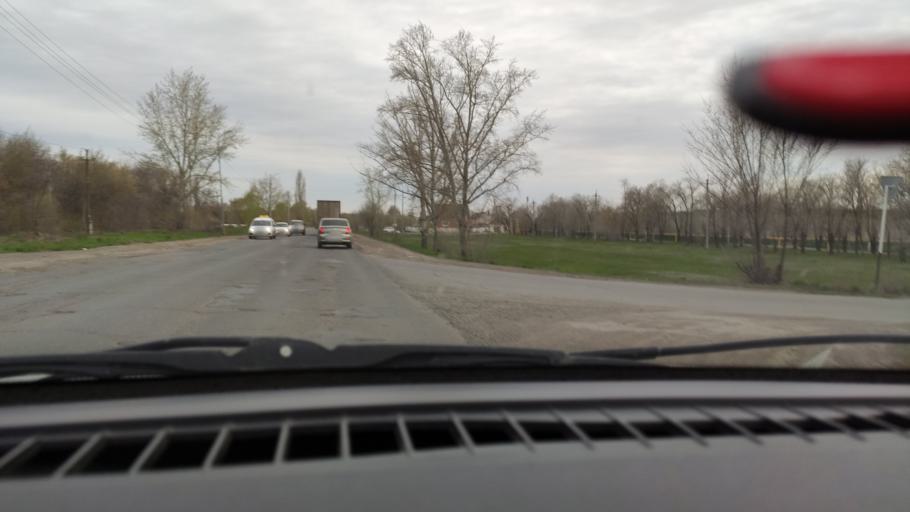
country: RU
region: Orenburg
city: Tatarskaya Kargala
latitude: 51.8651
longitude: 55.1392
